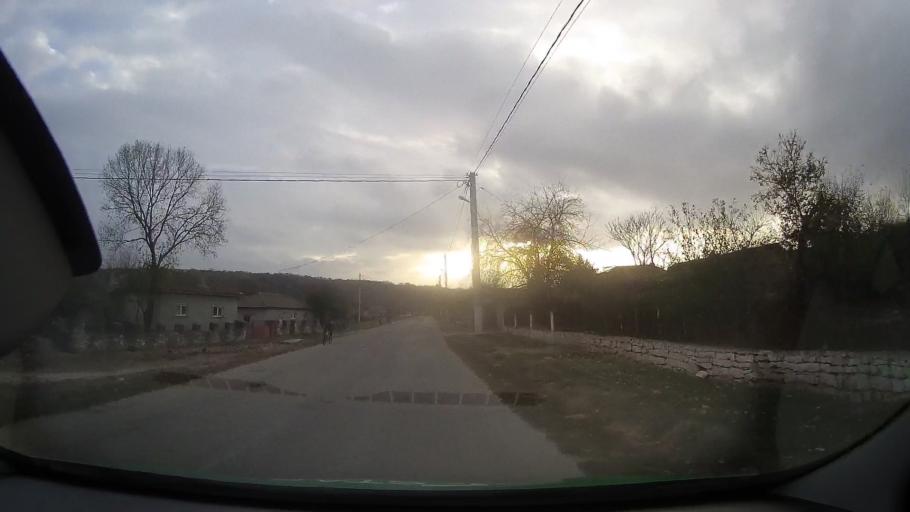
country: RO
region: Constanta
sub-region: Comuna Adamclisi
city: Adamclisi
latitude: 44.0424
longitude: 27.9551
